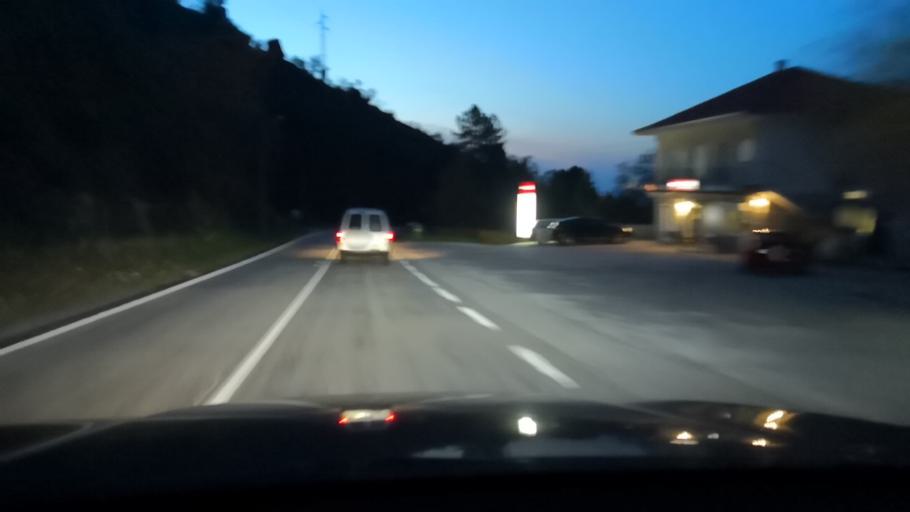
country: PT
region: Porto
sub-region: Baiao
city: Baiao
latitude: 41.2324
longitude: -8.0137
